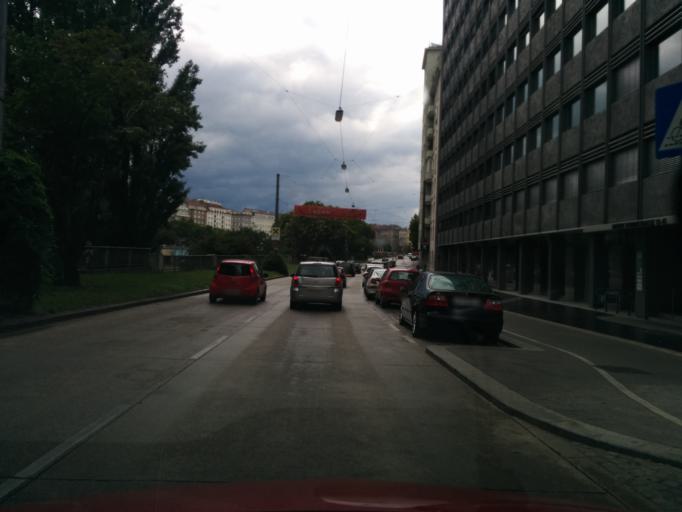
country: AT
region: Vienna
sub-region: Wien Stadt
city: Vienna
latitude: 48.2124
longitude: 16.3825
